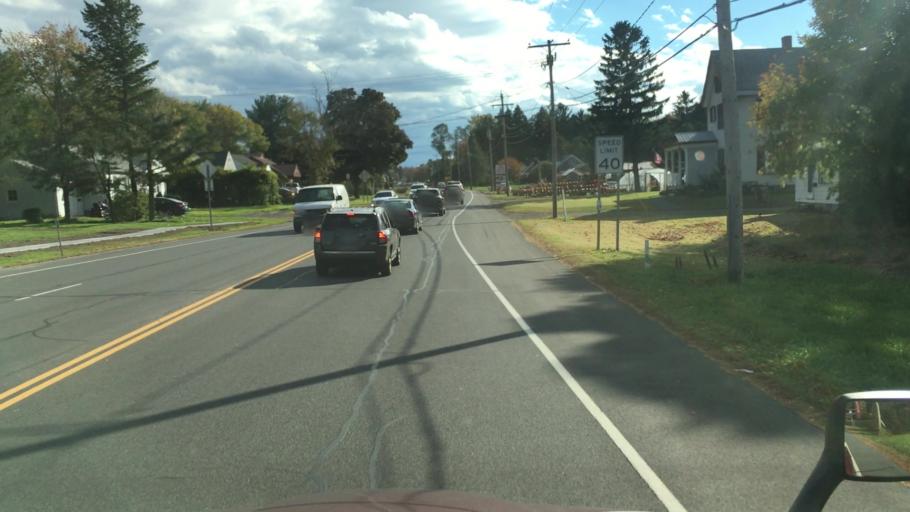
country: US
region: New York
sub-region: Schenectady County
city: East Glenville
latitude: 42.8664
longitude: -73.9328
